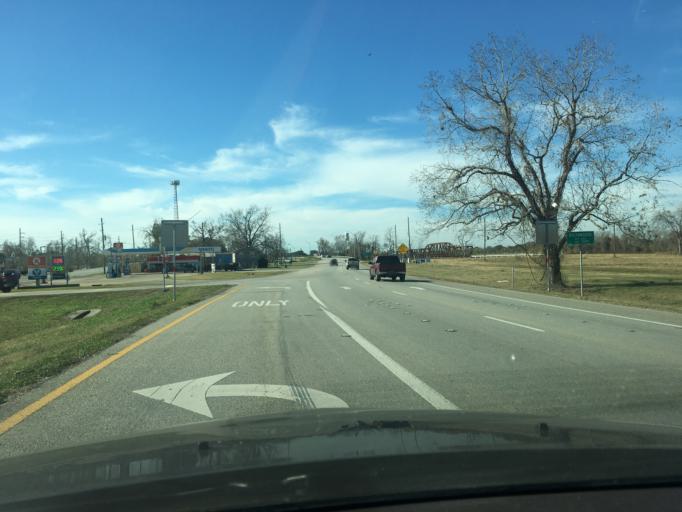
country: US
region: Texas
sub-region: Fort Bend County
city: Richmond
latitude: 29.5856
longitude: -95.7531
